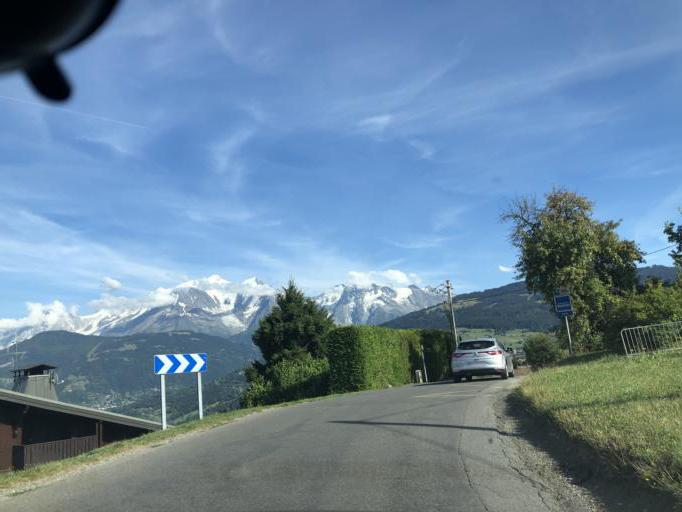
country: FR
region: Rhone-Alpes
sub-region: Departement de la Haute-Savoie
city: Cordon
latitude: 45.9122
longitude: 6.6253
